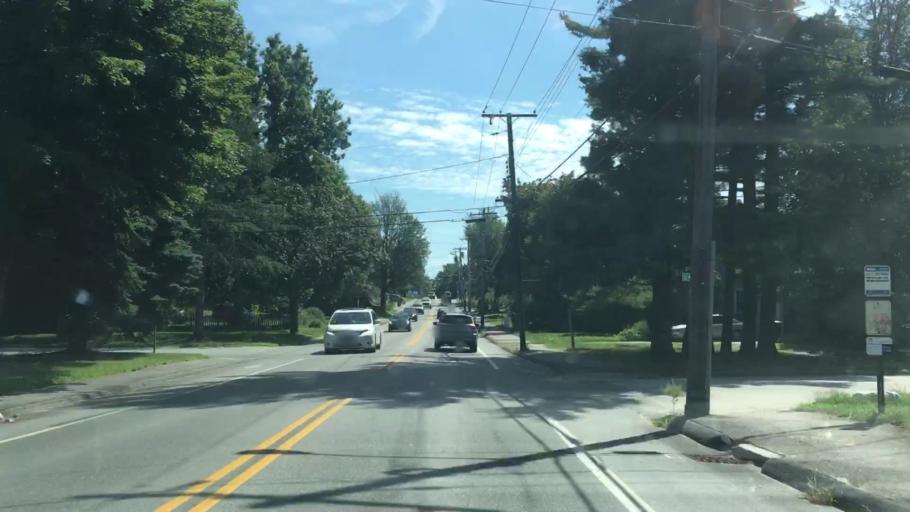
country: US
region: Maine
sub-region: Cumberland County
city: South Portland
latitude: 43.6275
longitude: -70.2508
